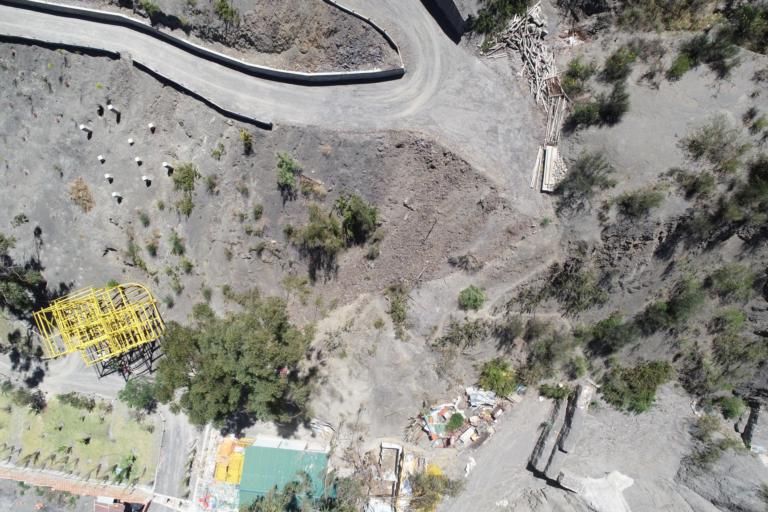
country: BO
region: La Paz
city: La Paz
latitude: -16.6245
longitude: -68.0524
